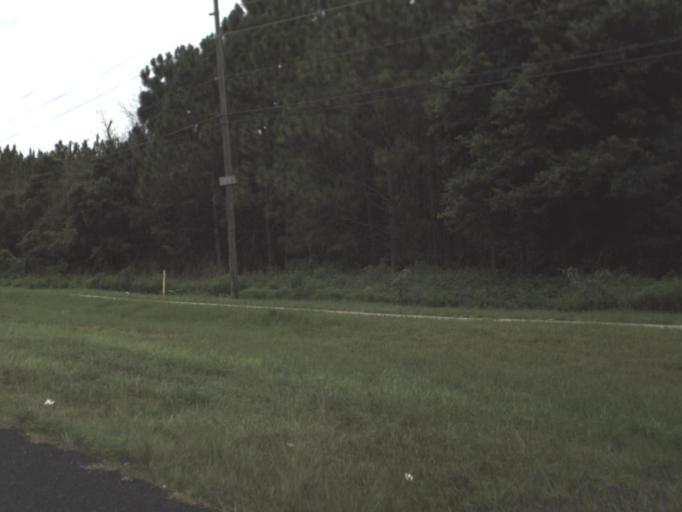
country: US
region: Florida
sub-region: Citrus County
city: Inverness Highlands North
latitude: 28.8558
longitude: -82.4003
